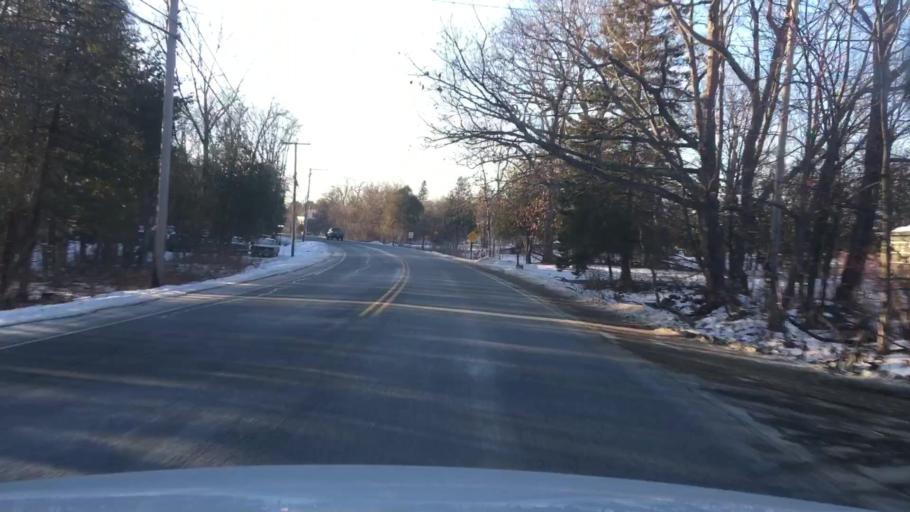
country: US
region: Maine
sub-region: Penobscot County
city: Eddington
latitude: 44.8299
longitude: -68.6637
